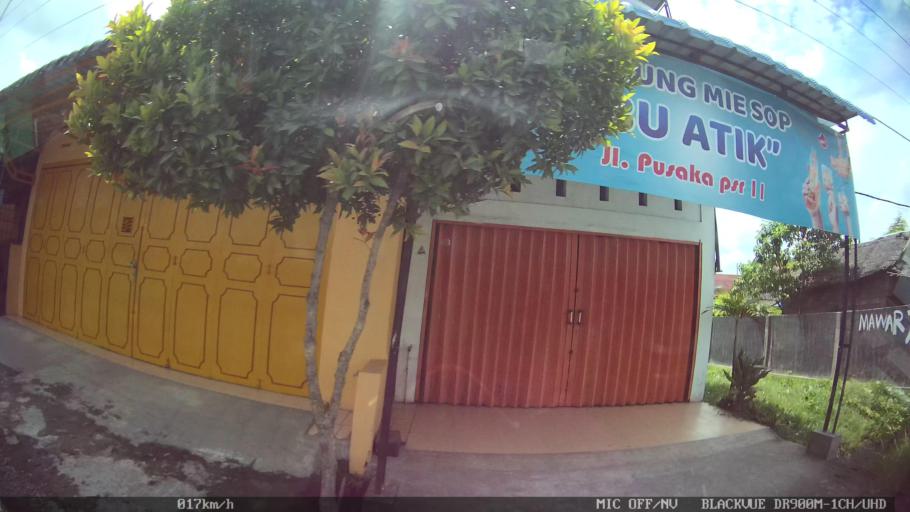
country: ID
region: North Sumatra
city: Medan
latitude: 3.6117
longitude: 98.7608
